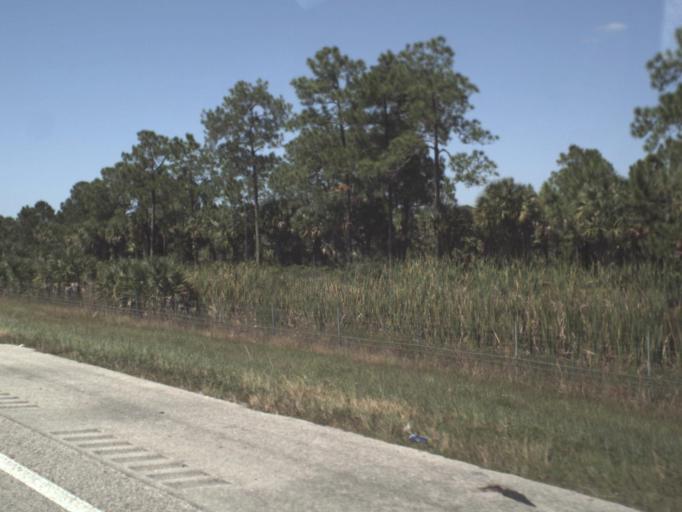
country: US
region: Florida
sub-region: Collier County
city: Golden Gate
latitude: 26.1533
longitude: -81.5605
